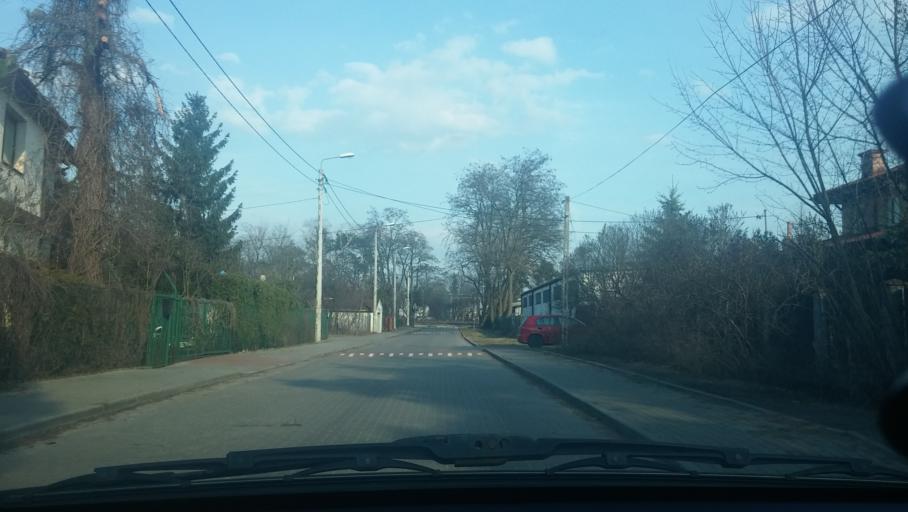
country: PL
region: Masovian Voivodeship
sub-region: Powiat otwocki
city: Jozefow
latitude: 52.1626
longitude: 21.2075
